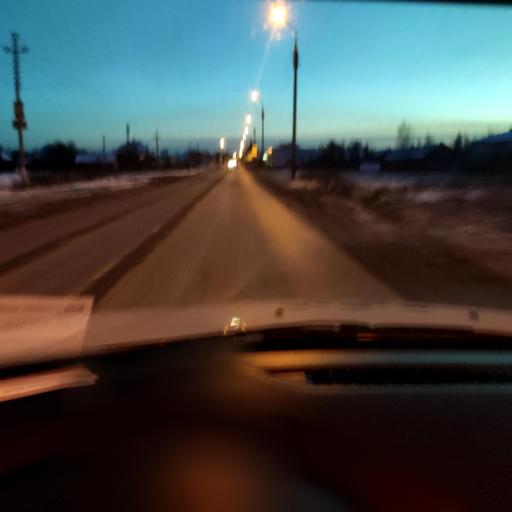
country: RU
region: Samara
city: Tol'yatti
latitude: 53.5654
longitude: 49.3966
